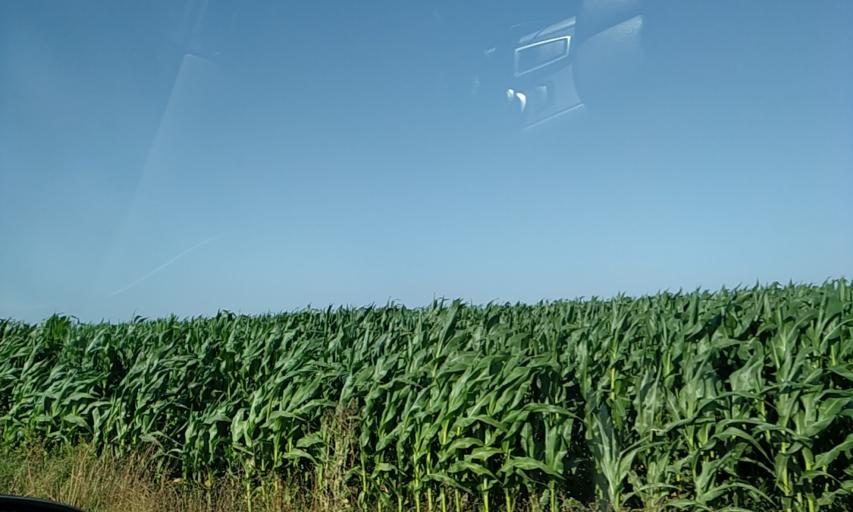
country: PT
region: Santarem
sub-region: Almeirim
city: Fazendas de Almeirim
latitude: 39.1535
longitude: -8.6194
